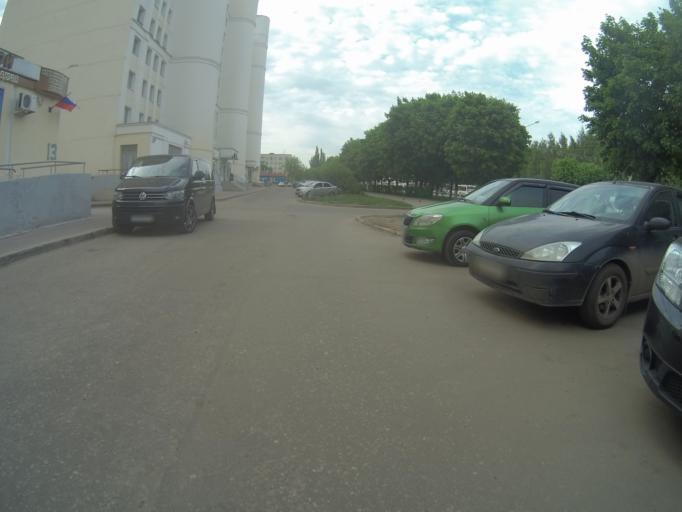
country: RU
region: Vladimir
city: Kommunar
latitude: 56.1664
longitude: 40.4651
